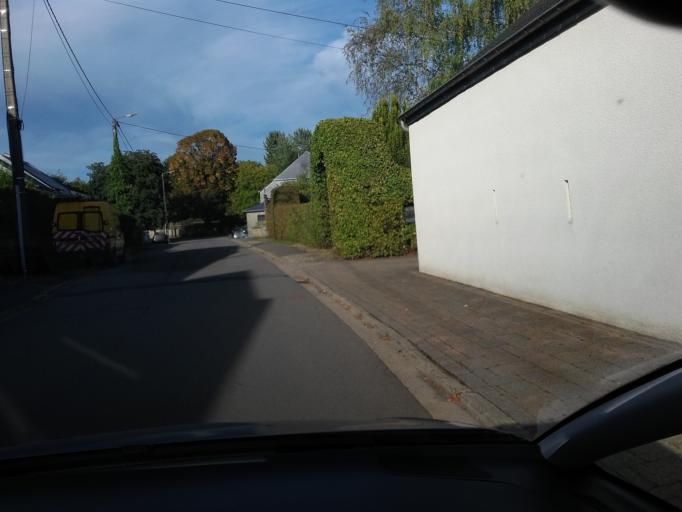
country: BE
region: Wallonia
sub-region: Province du Luxembourg
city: Attert
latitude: 49.7552
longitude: 5.7253
